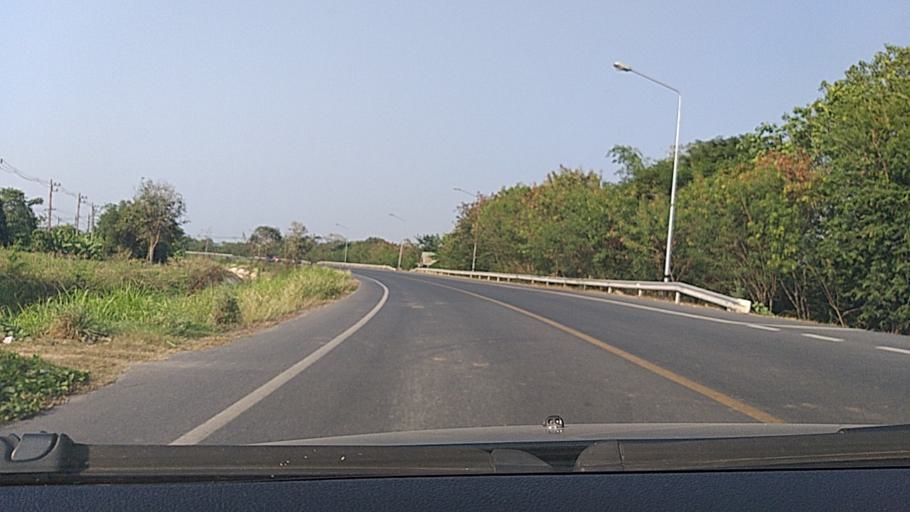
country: TH
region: Sing Buri
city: Phrom Buri
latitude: 14.8113
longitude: 100.4354
